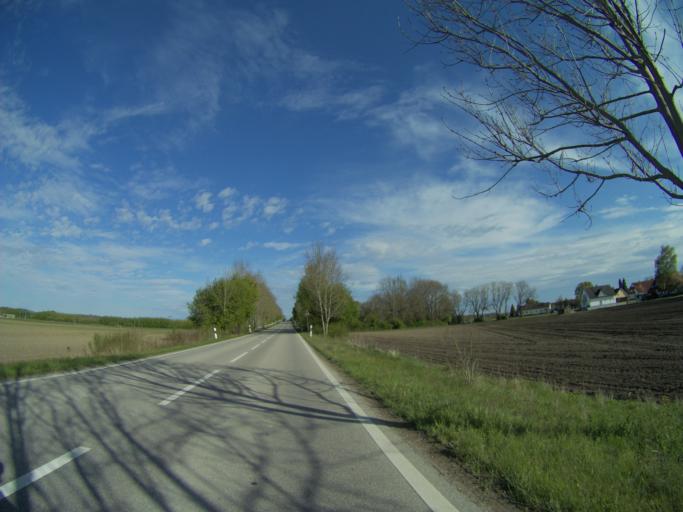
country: DE
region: Bavaria
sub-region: Upper Bavaria
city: Freising
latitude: 48.3694
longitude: 11.7085
